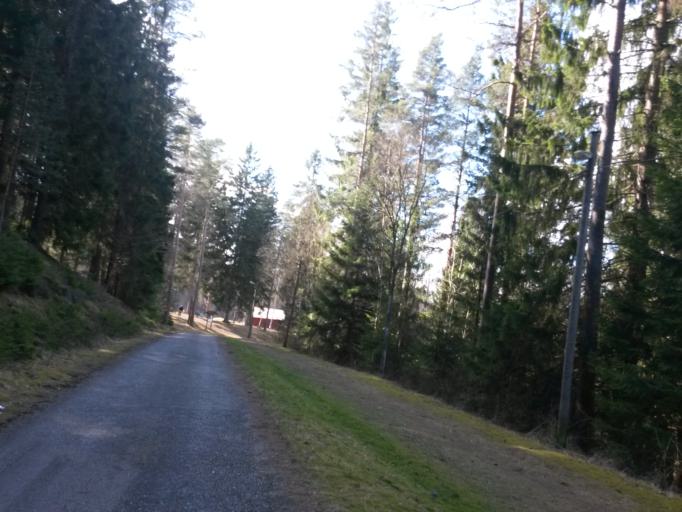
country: SE
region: Vaestra Goetaland
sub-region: Vargarda Kommun
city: Vargarda
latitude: 58.0355
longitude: 12.8287
